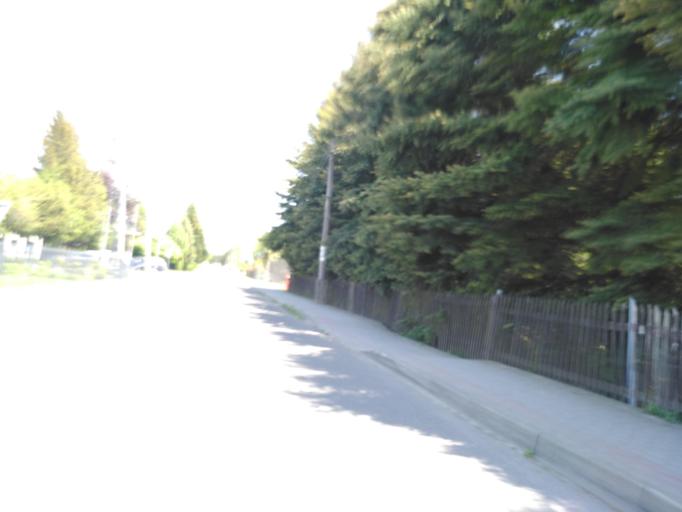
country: PL
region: Subcarpathian Voivodeship
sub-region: Powiat krosnienski
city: Jedlicze
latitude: 49.6979
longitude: 21.6786
